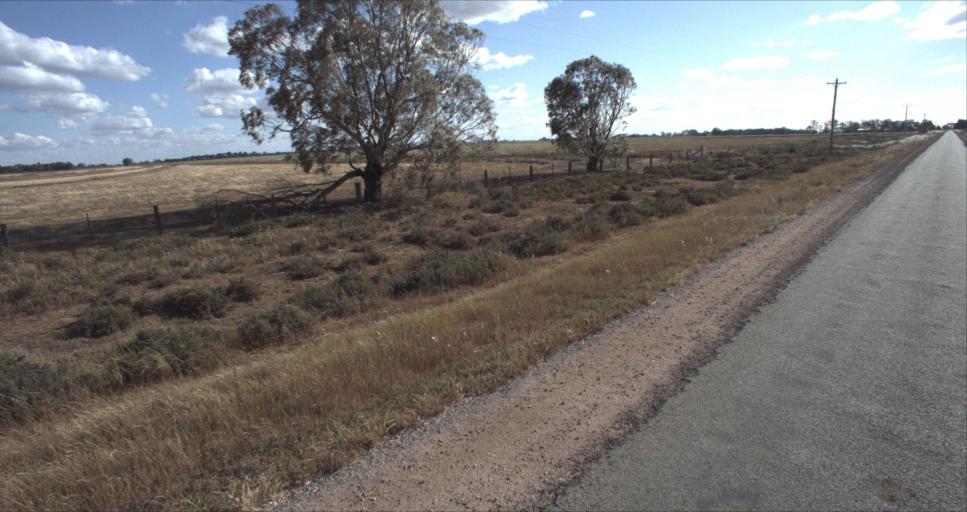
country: AU
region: New South Wales
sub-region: Leeton
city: Leeton
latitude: -34.4589
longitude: 146.2616
